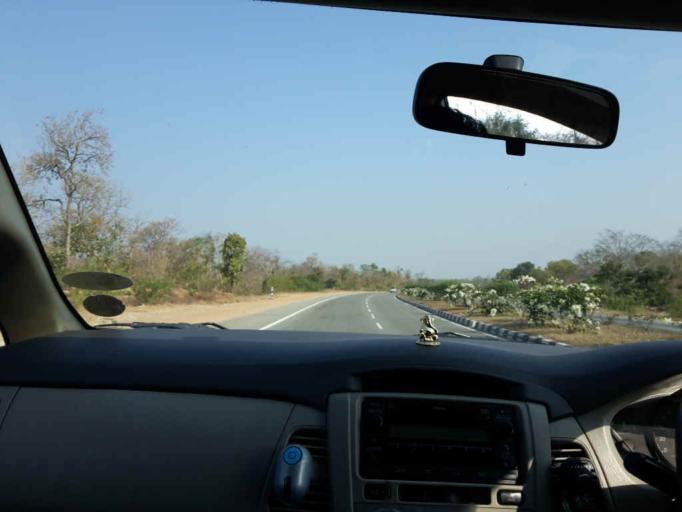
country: IN
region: Telangana
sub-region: Nizamabad District
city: Kamareddi
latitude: 18.4848
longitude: 78.2181
